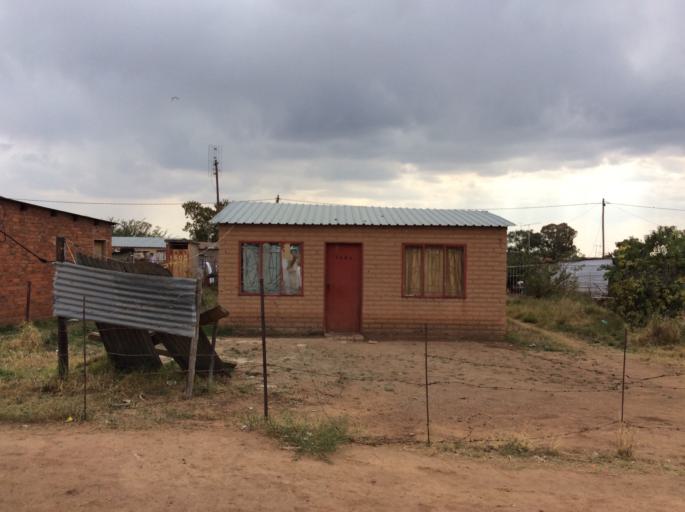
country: ZA
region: Orange Free State
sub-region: Xhariep District Municipality
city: Dewetsdorp
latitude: -29.5758
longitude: 26.6837
